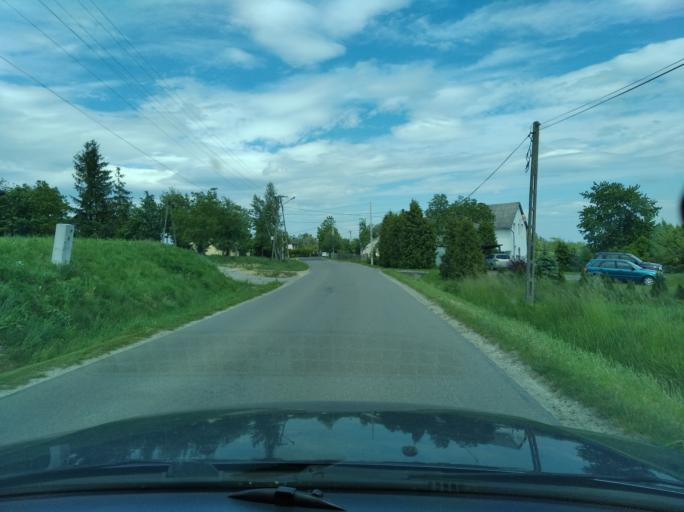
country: PL
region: Subcarpathian Voivodeship
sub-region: Powiat ropczycko-sedziszowski
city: Ropczyce
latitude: 50.0282
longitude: 21.6097
